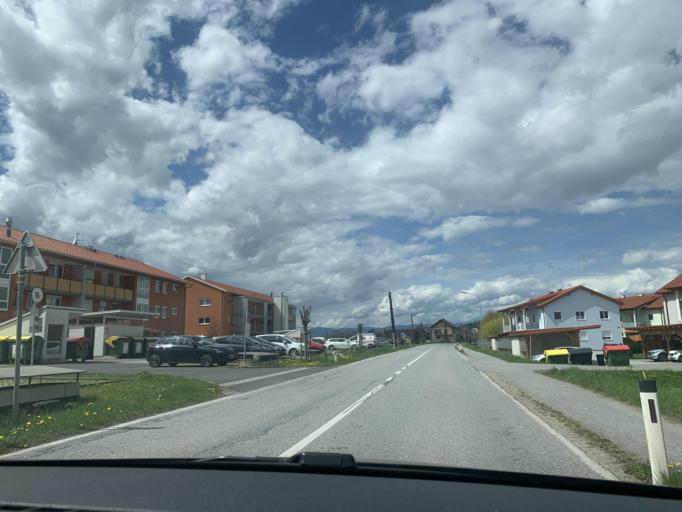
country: AT
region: Styria
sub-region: Politischer Bezirk Graz-Umgebung
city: Unterpremstatten
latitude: 46.9487
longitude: 15.3735
